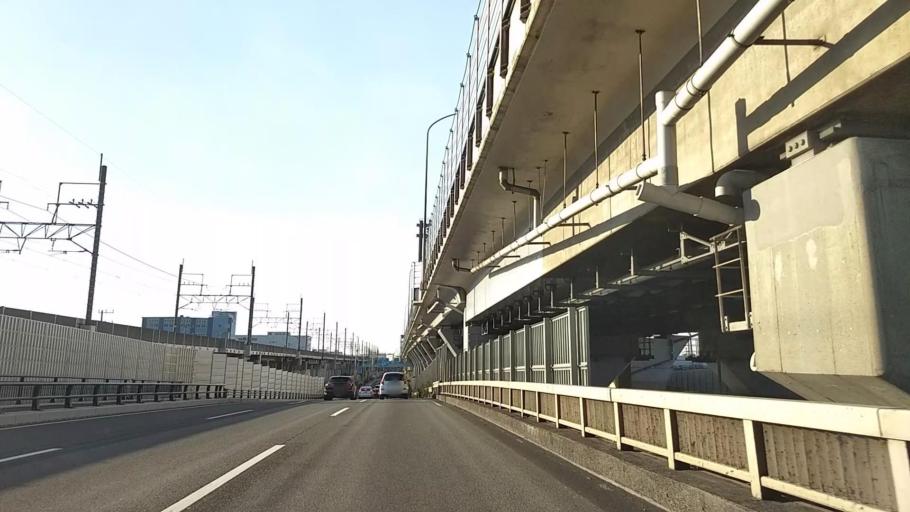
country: JP
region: Chiba
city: Funabashi
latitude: 35.6883
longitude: 139.9770
